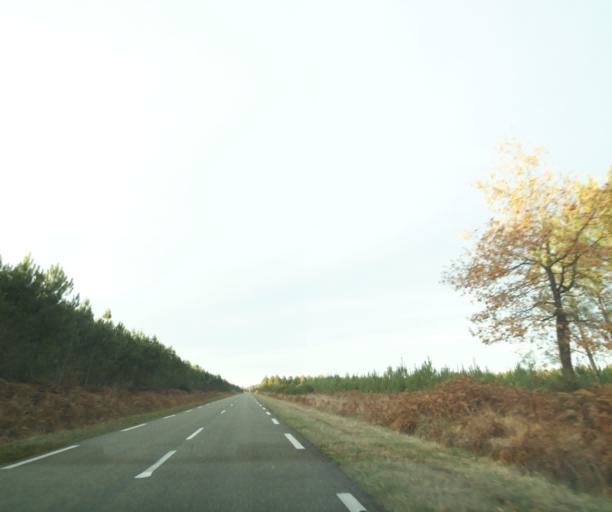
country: FR
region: Aquitaine
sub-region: Departement des Landes
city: Roquefort
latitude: 44.1810
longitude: -0.1465
